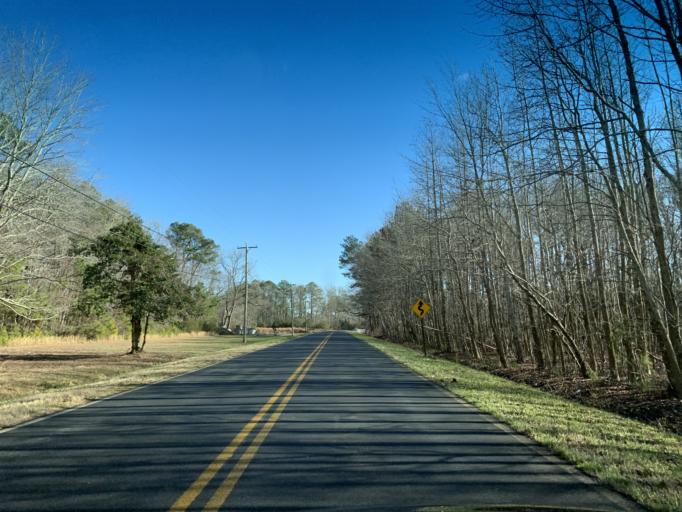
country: US
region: Maryland
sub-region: Worcester County
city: Ocean Pines
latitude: 38.4164
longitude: -75.1240
